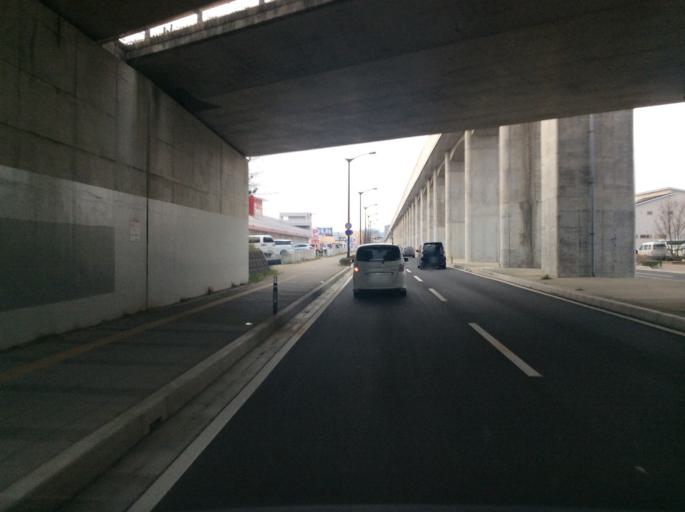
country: JP
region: Miyagi
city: Iwanuma
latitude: 38.1626
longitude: 140.9066
